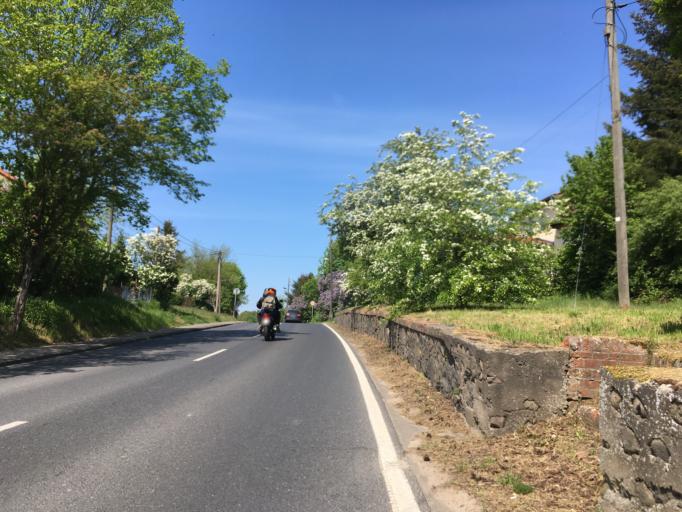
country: DE
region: Brandenburg
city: Rudnitz
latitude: 52.7617
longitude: 13.5657
